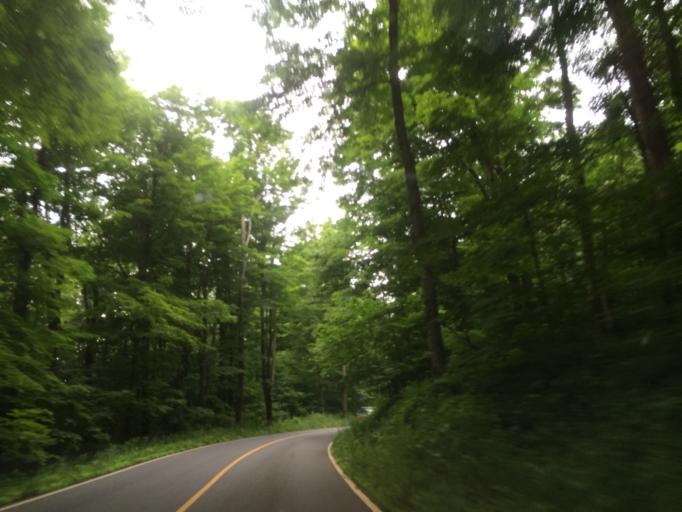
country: US
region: Massachusetts
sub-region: Berkshire County
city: Adams
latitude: 42.6109
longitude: -73.2002
